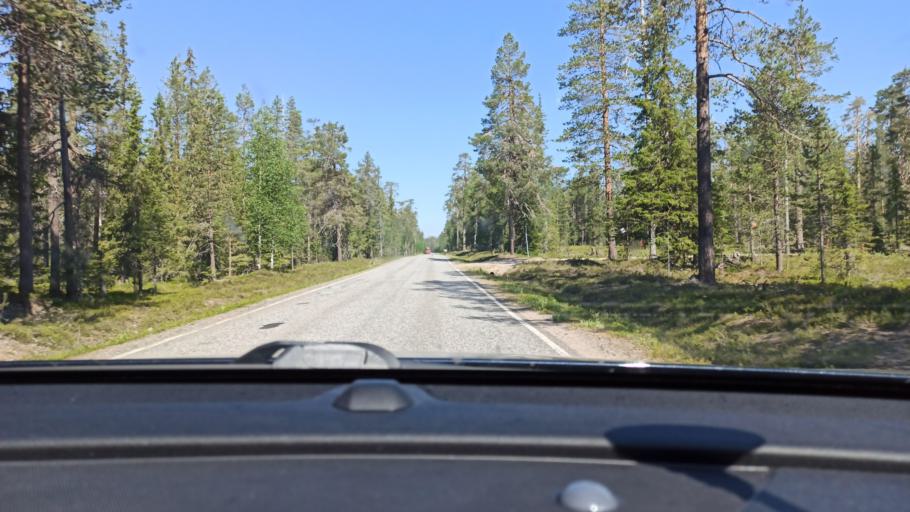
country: FI
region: Lapland
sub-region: Tunturi-Lappi
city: Kolari
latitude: 67.6623
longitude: 24.1645
